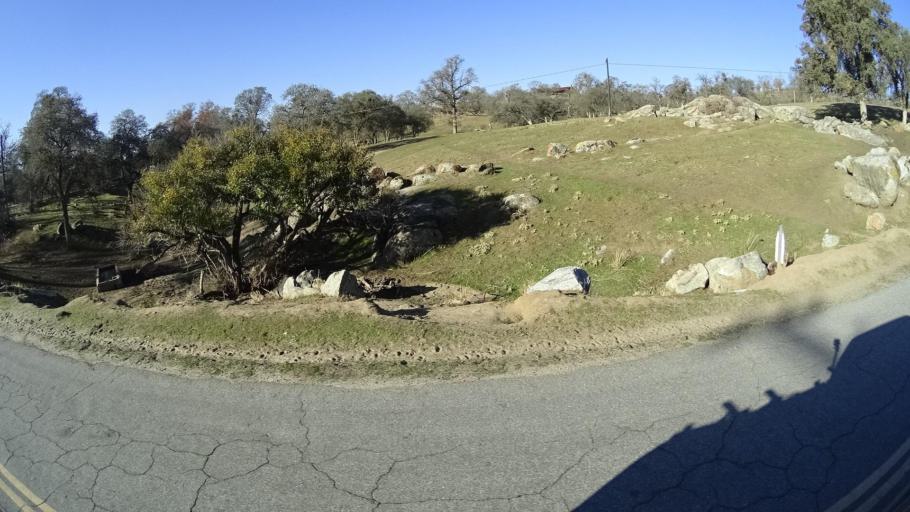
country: US
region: California
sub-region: Kern County
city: Alta Sierra
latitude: 35.7504
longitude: -118.8186
